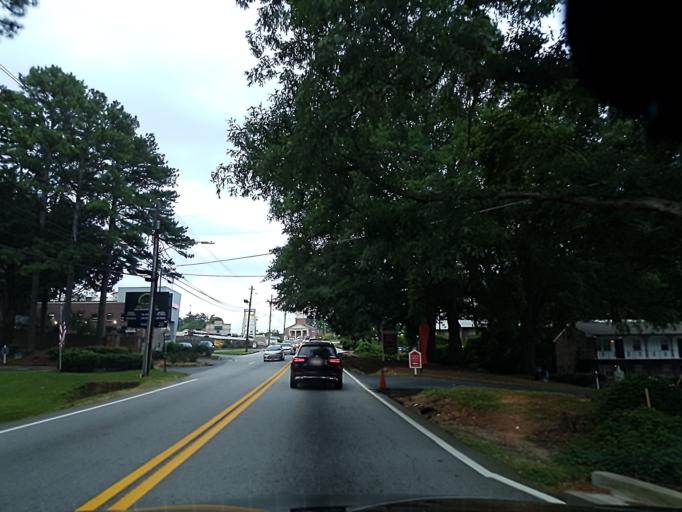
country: US
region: Georgia
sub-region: DeKalb County
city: North Druid Hills
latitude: 33.8183
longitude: -84.3353
